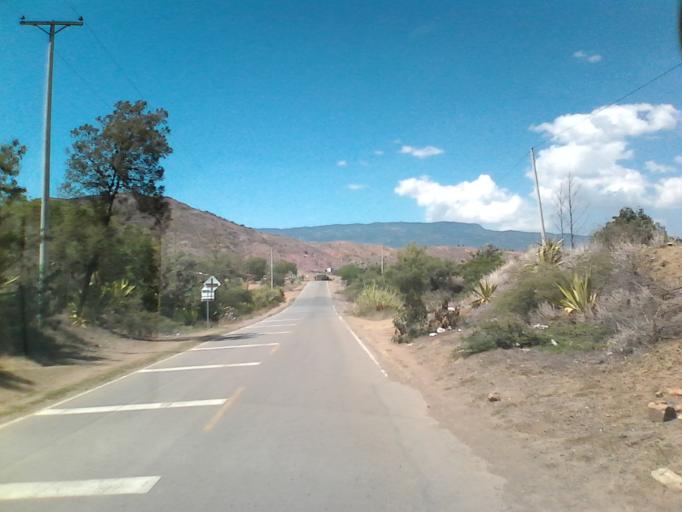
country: CO
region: Boyaca
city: Sachica
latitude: 5.6068
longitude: -73.5603
